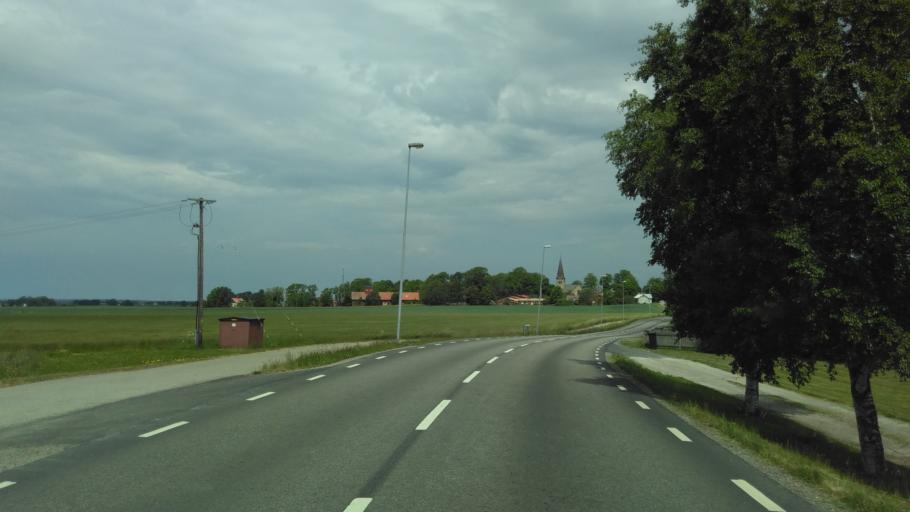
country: SE
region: Vaestra Goetaland
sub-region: Vara Kommun
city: Kvanum
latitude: 58.3754
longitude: 13.1479
